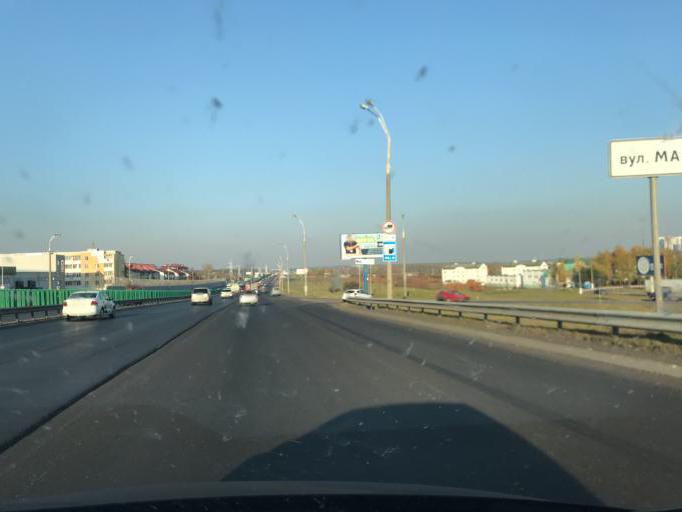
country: BY
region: Minsk
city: Zhdanovichy
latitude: 53.9362
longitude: 27.4272
